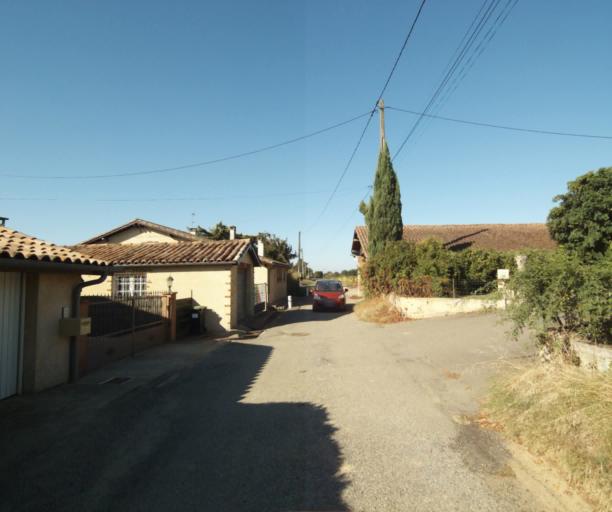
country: FR
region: Midi-Pyrenees
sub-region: Departement du Tarn-et-Garonne
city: Verdun-sur-Garonne
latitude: 43.8604
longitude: 1.2252
